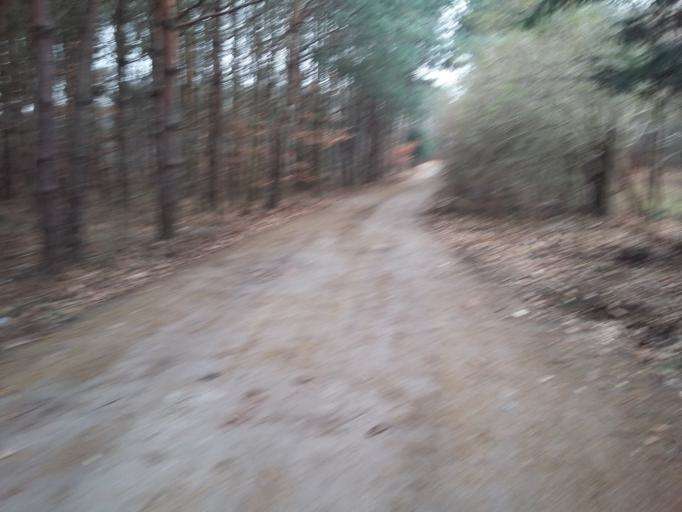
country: PL
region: Lodz Voivodeship
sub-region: Powiat pabianicki
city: Ksawerow
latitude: 51.7271
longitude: 19.3832
